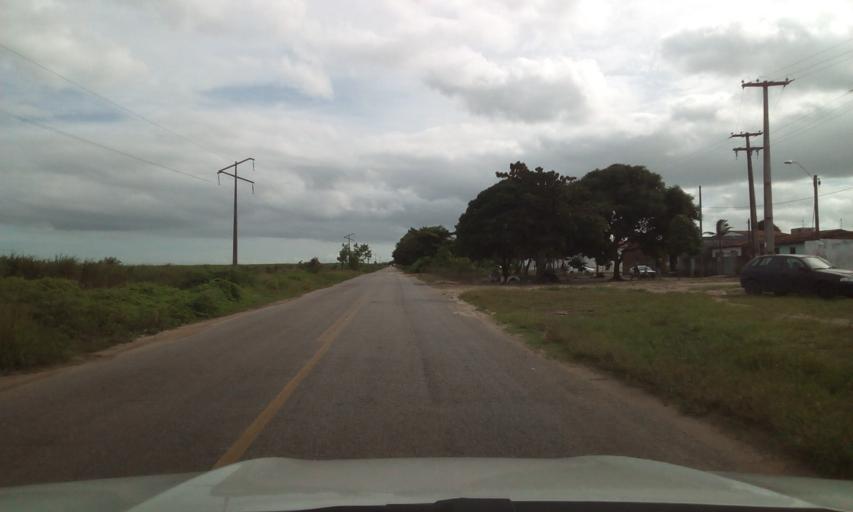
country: BR
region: Paraiba
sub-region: Santa Rita
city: Santa Rita
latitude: -6.9738
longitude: -34.9768
